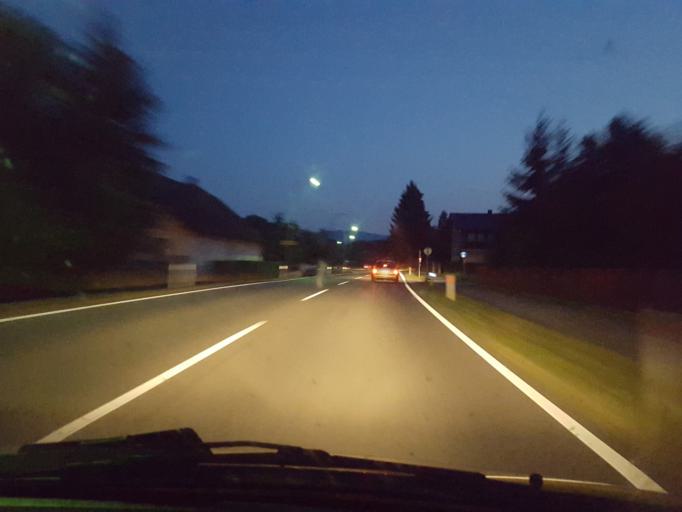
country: AT
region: Lower Austria
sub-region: Politischer Bezirk Scheibbs
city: Wieselburg
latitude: 48.1042
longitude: 15.1364
